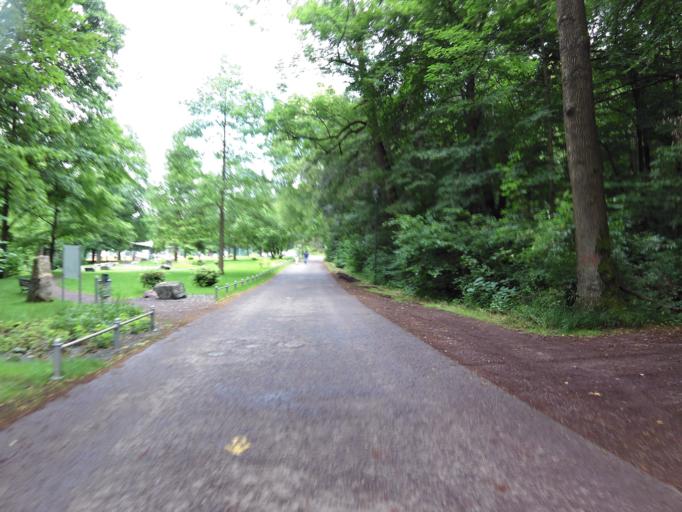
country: DE
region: Thuringia
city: Tabarz
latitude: 50.8669
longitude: 10.5101
